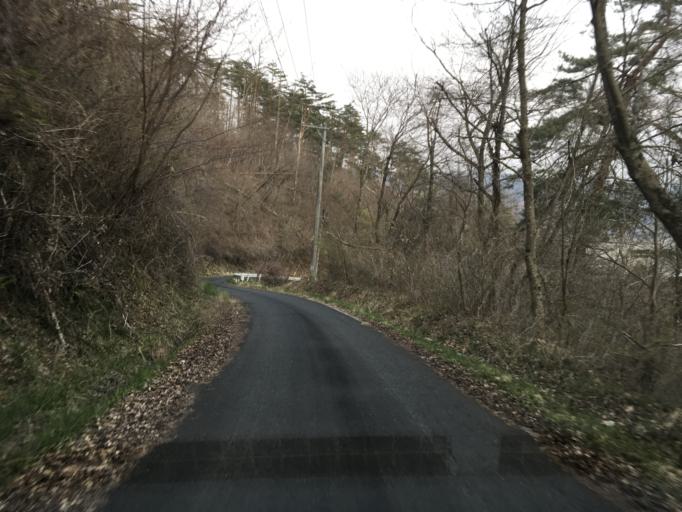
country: JP
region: Iwate
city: Ichinoseki
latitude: 38.9421
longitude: 141.2346
